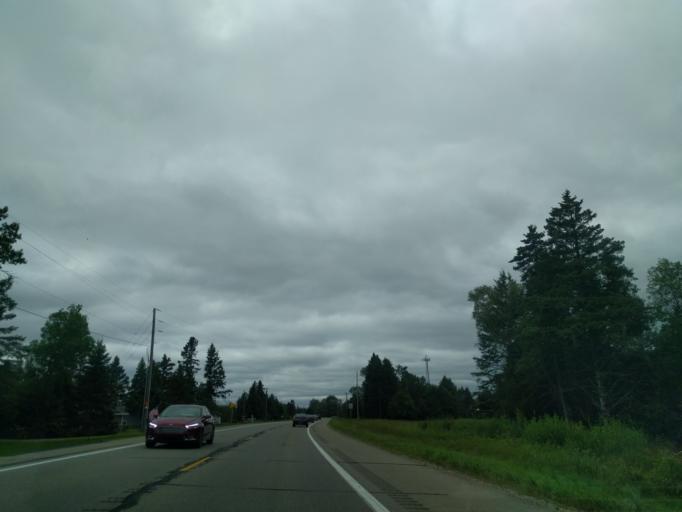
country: US
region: Michigan
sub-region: Delta County
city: Escanaba
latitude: 45.6428
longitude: -87.1913
